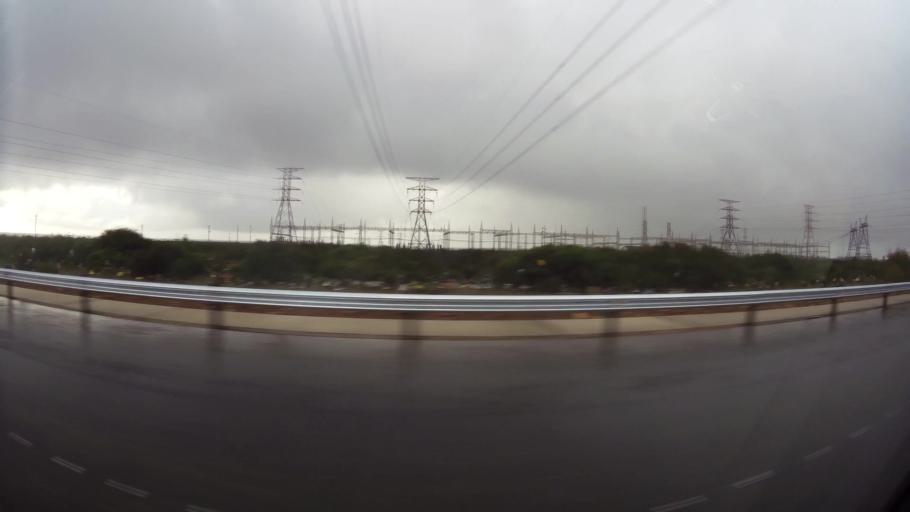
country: ZA
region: Eastern Cape
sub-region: Nelson Mandela Bay Metropolitan Municipality
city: Port Elizabeth
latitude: -33.8370
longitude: 25.5206
